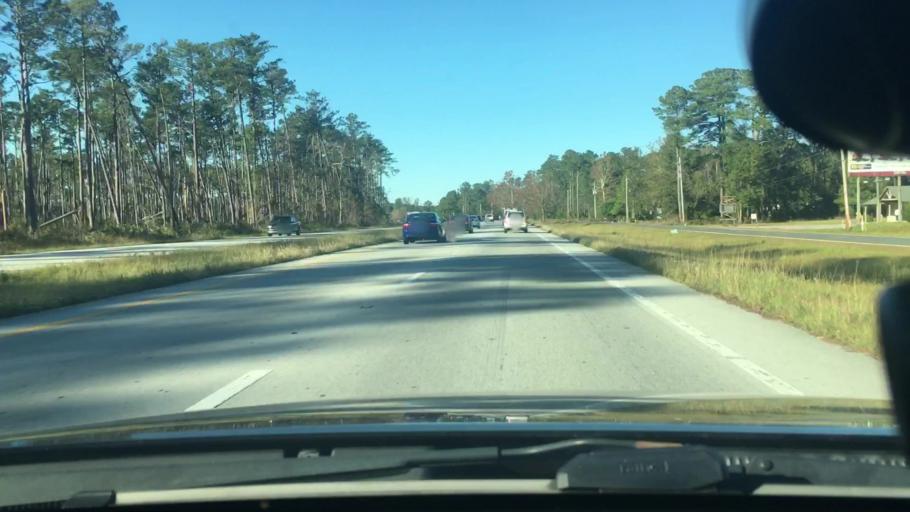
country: US
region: North Carolina
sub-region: Craven County
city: Neuse Forest
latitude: 34.9434
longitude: -76.9487
